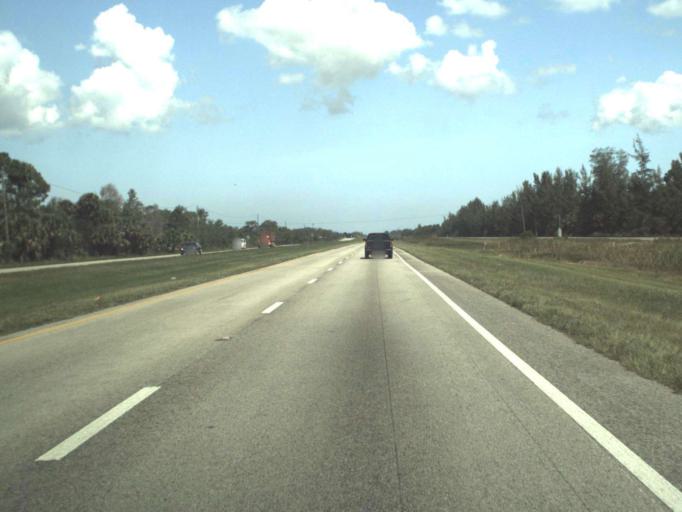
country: US
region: Florida
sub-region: Palm Beach County
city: Palm Beach Gardens
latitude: 26.8272
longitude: -80.1784
